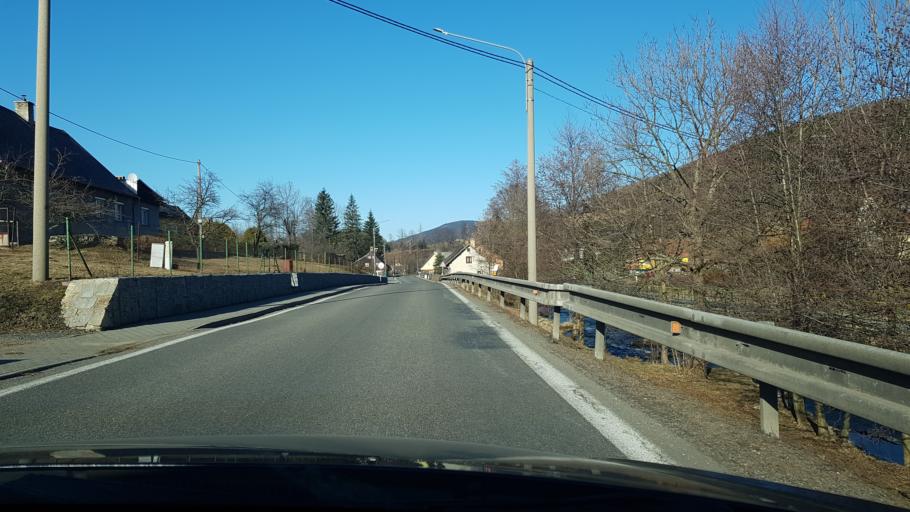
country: CZ
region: Olomoucky
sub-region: Okres Jesenik
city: Jesenik
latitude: 50.1756
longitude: 17.1979
